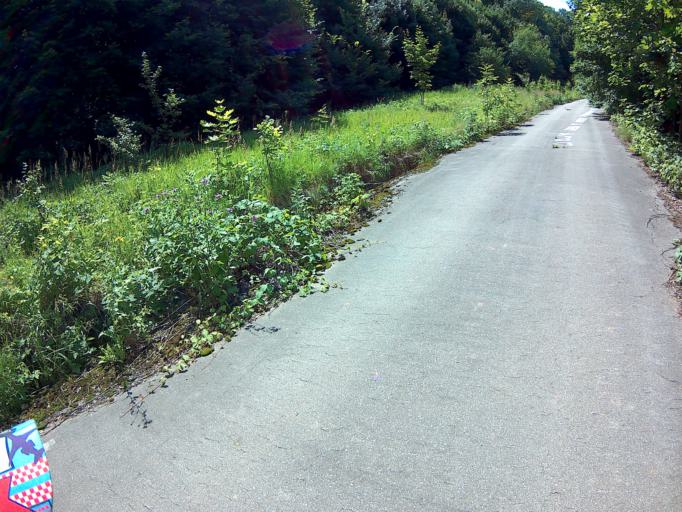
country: RU
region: Nizjnij Novgorod
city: Nizhniy Novgorod
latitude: 56.2348
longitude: 43.9331
